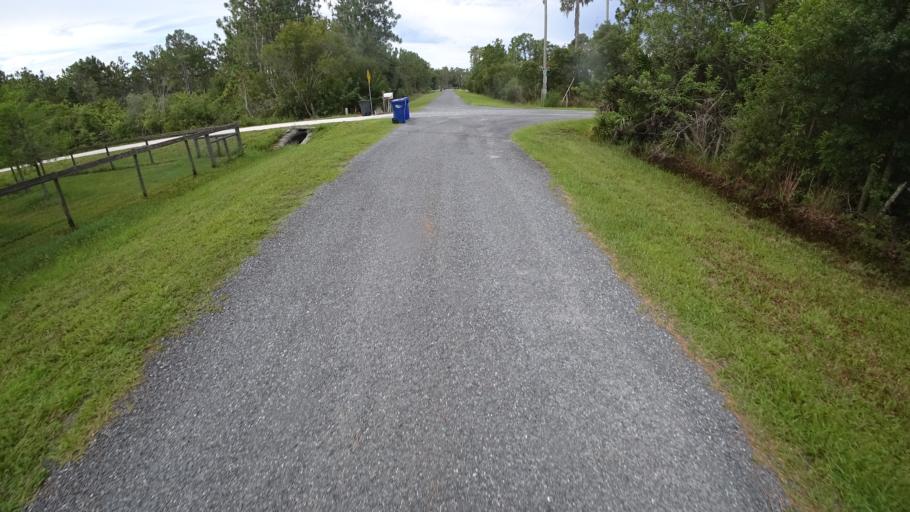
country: US
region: Florida
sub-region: Sarasota County
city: Lake Sarasota
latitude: 27.3978
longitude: -82.2794
